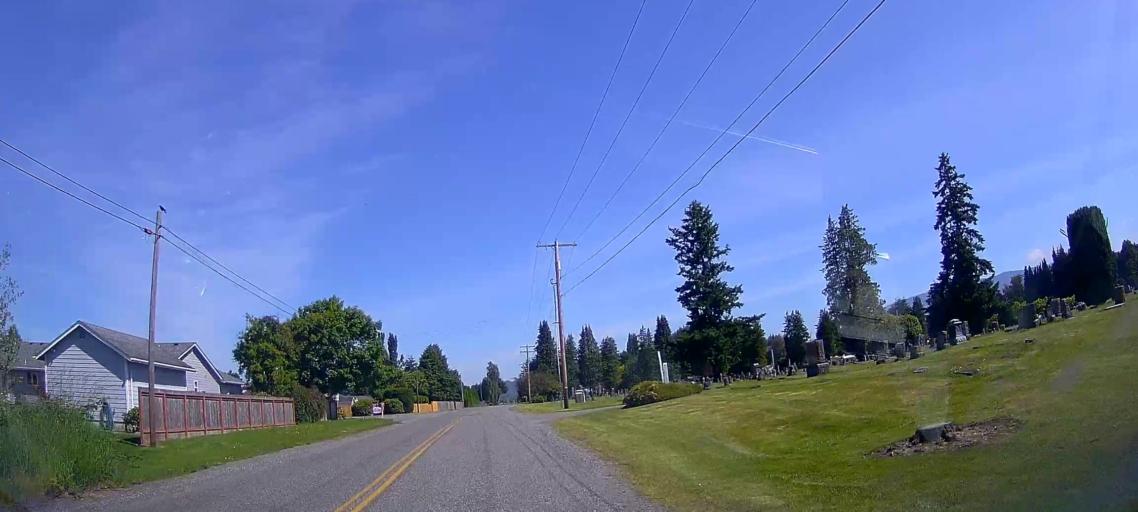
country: US
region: Washington
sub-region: Skagit County
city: Burlington
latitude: 48.4842
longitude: -122.3084
